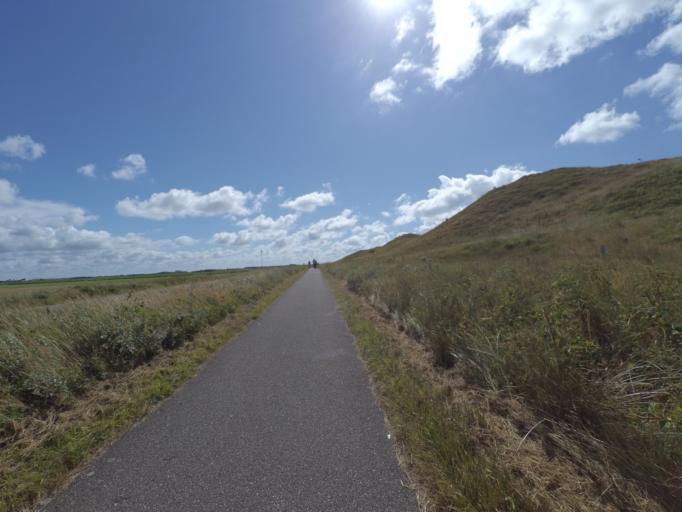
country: NL
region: North Holland
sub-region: Gemeente Texel
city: Den Burg
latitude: 53.1213
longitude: 4.8055
